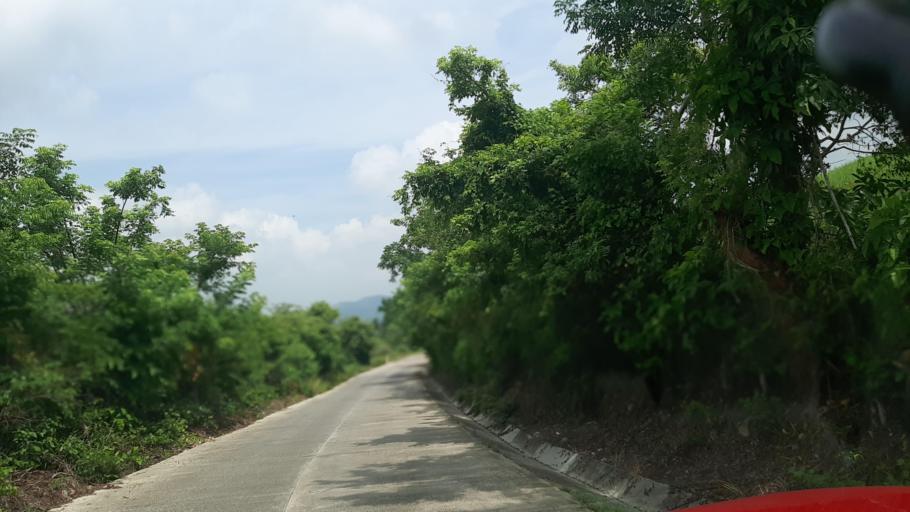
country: MX
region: Veracruz
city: Gutierrez Zamora
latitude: 20.4463
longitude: -97.1748
